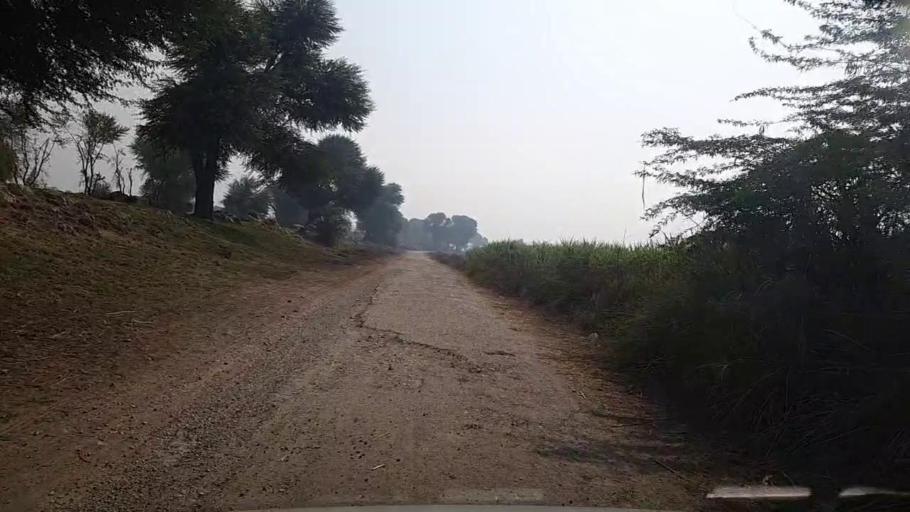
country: PK
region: Sindh
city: Setharja Old
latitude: 27.1335
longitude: 68.5115
